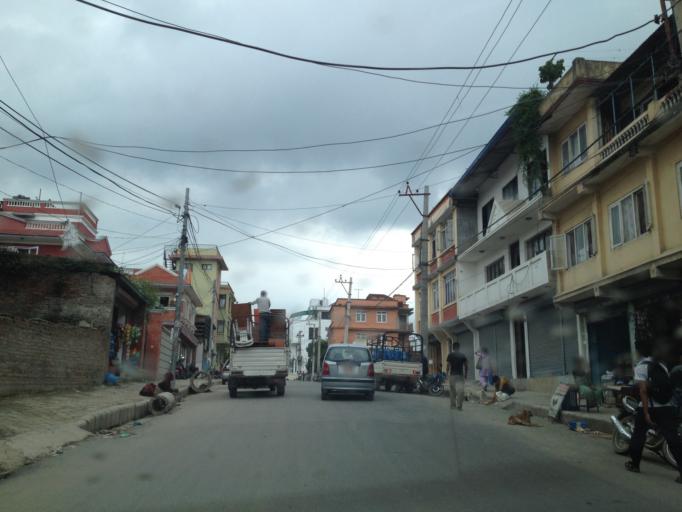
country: NP
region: Central Region
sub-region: Bagmati Zone
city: Kathmandu
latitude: 27.7033
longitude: 85.2986
